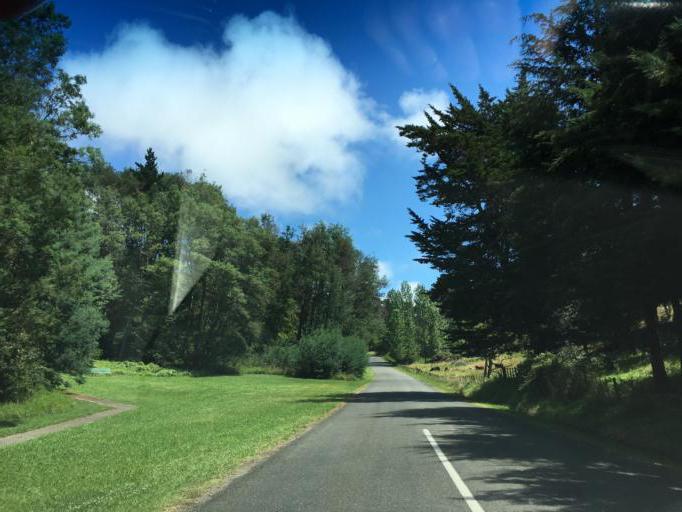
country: NZ
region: Hawke's Bay
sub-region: Wairoa District
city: Wairoa
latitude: -39.0450
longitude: 177.4163
